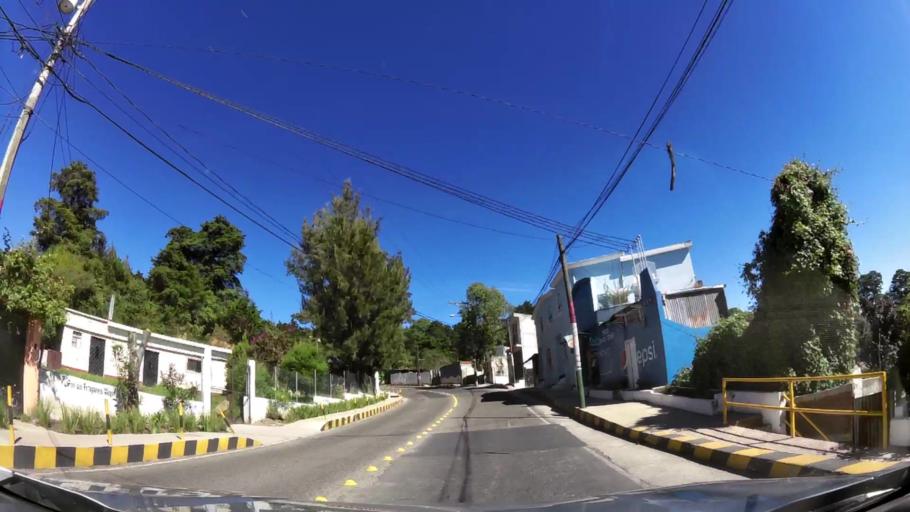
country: GT
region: Guatemala
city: Fraijanes
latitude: 14.4746
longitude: -90.4507
